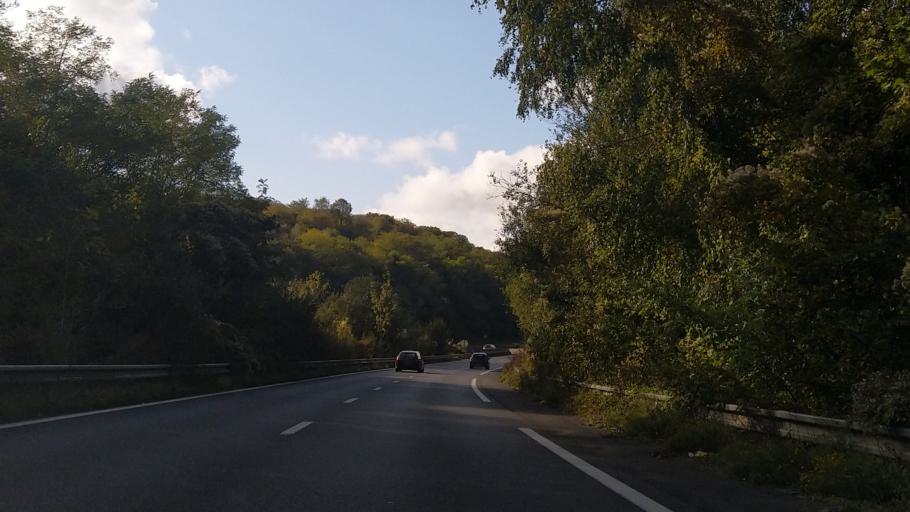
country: FR
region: Ile-de-France
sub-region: Departement du Val-d'Oise
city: Meriel
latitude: 49.0737
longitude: 2.2400
